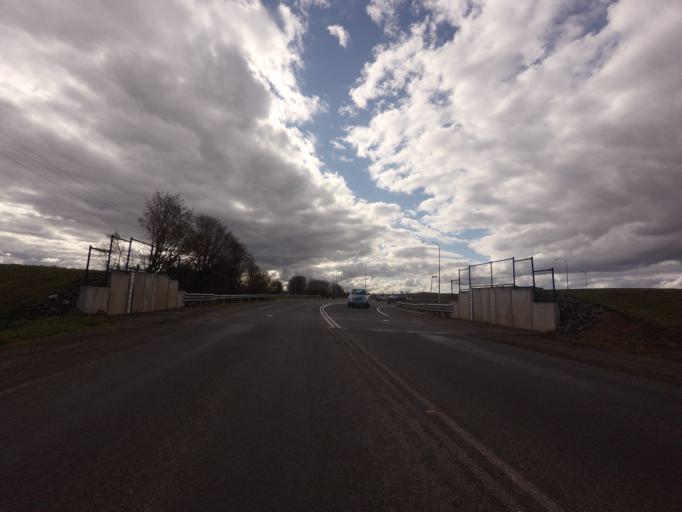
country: AU
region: Tasmania
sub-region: Northern Midlands
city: Longford
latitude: -41.5851
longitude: 147.1168
